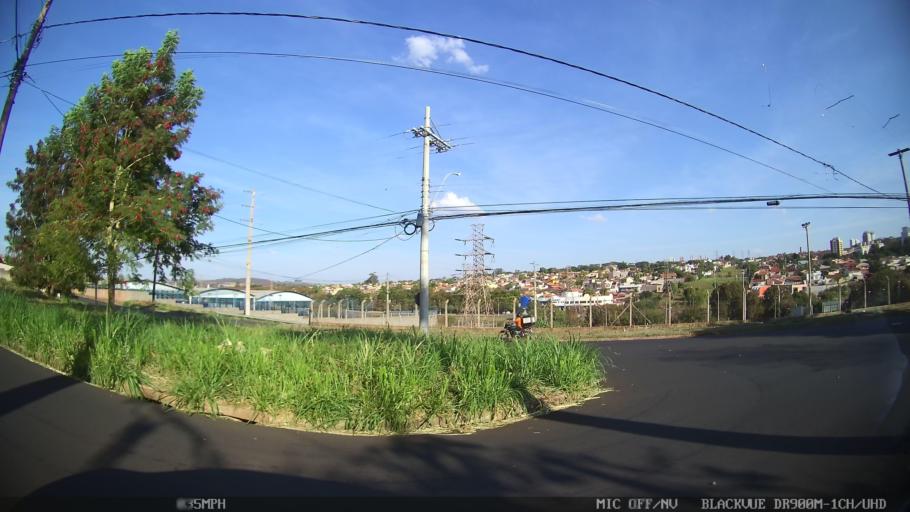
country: BR
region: Sao Paulo
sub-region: Ribeirao Preto
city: Ribeirao Preto
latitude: -21.2079
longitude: -47.7848
